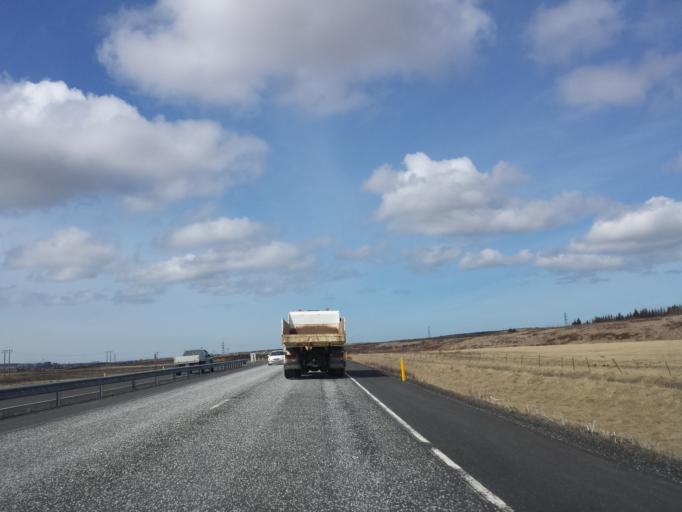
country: IS
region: Capital Region
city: Mosfellsbaer
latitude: 64.0866
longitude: -21.6887
